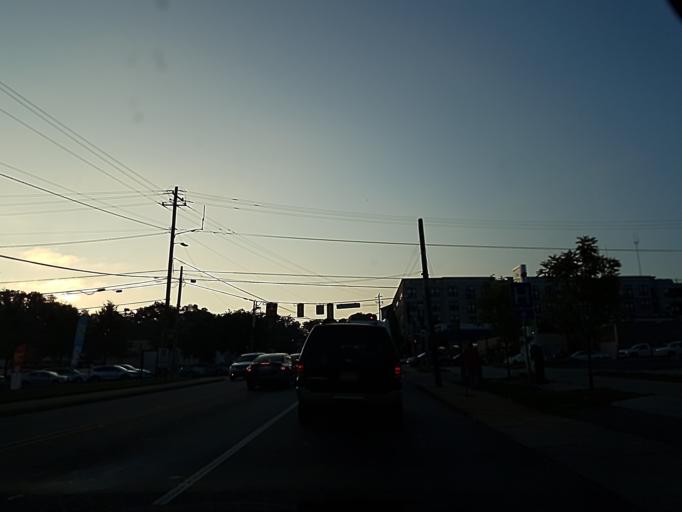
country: US
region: Georgia
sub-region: DeKalb County
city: North Druid Hills
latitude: 33.8186
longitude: -84.3523
